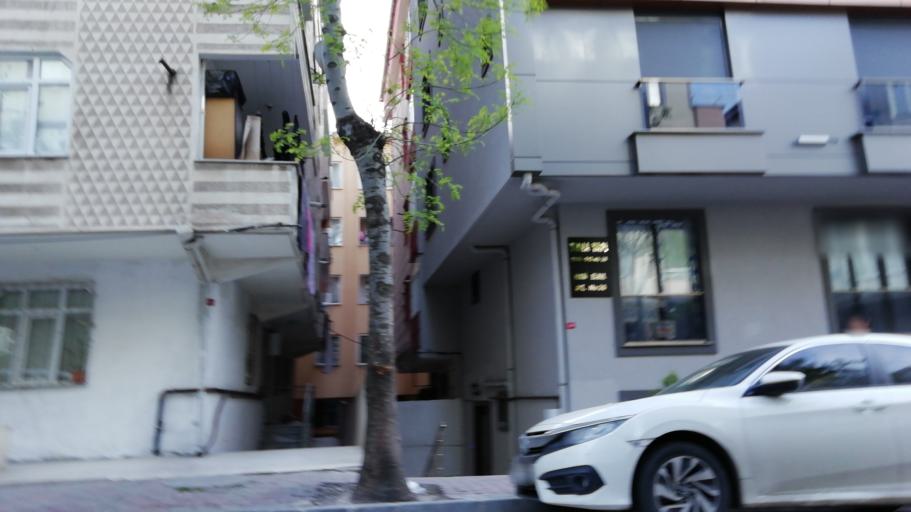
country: TR
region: Istanbul
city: Bagcilar
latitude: 41.0220
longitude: 28.8354
